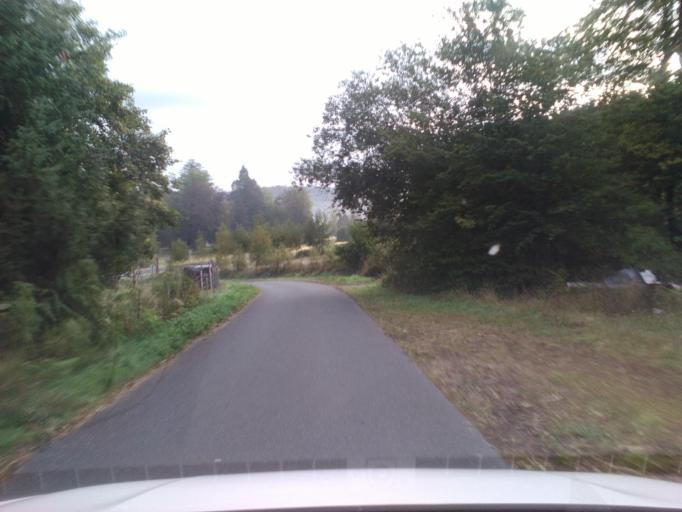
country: FR
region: Lorraine
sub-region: Departement des Vosges
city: Senones
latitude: 48.4091
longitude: 7.0404
